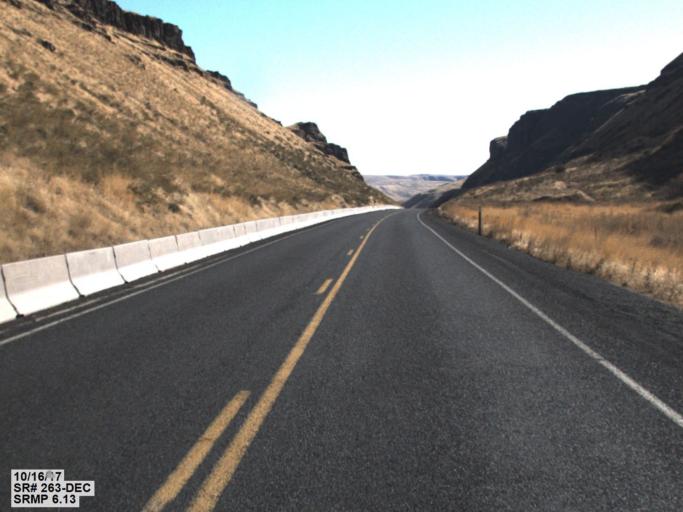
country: US
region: Washington
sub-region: Franklin County
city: Connell
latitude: 46.6029
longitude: -118.5507
